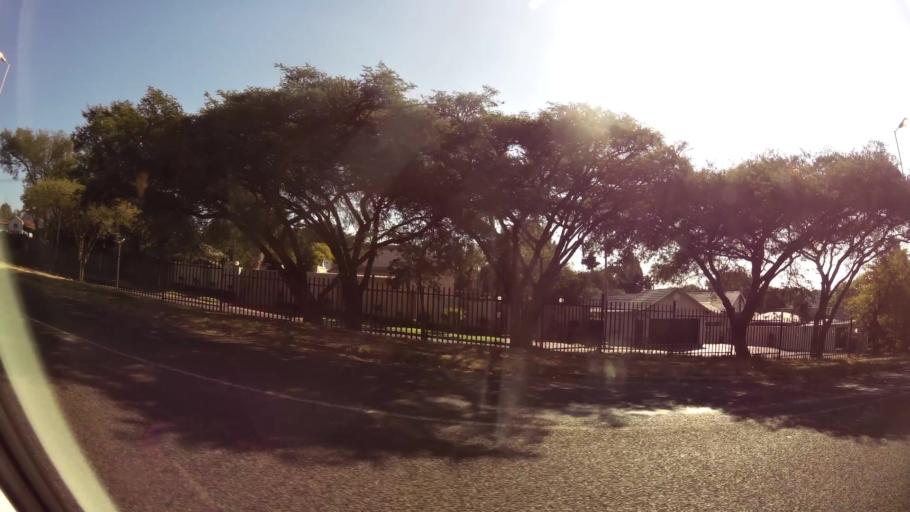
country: ZA
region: Gauteng
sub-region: City of Tshwane Metropolitan Municipality
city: Centurion
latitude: -25.8127
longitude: 28.2777
